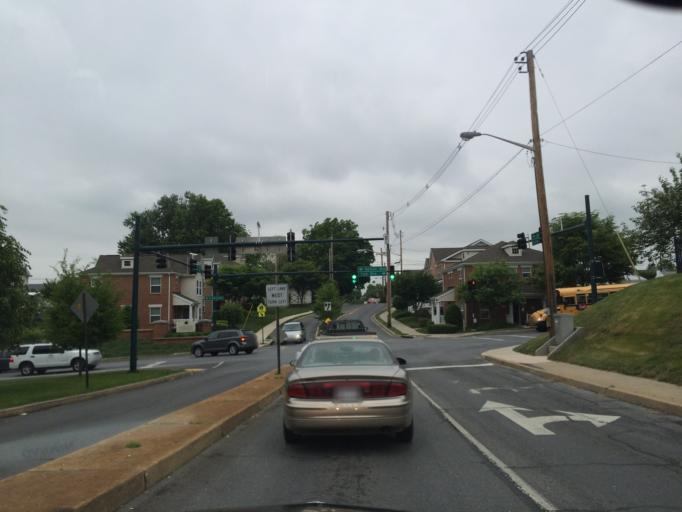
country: US
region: Maryland
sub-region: Washington County
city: Hagerstown
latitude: 39.6446
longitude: -77.7340
